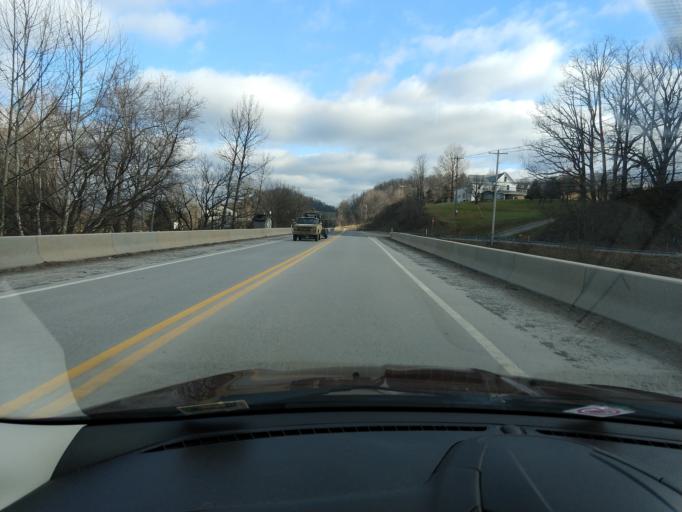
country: US
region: West Virginia
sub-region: Randolph County
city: Elkins
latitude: 38.8090
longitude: -79.8824
